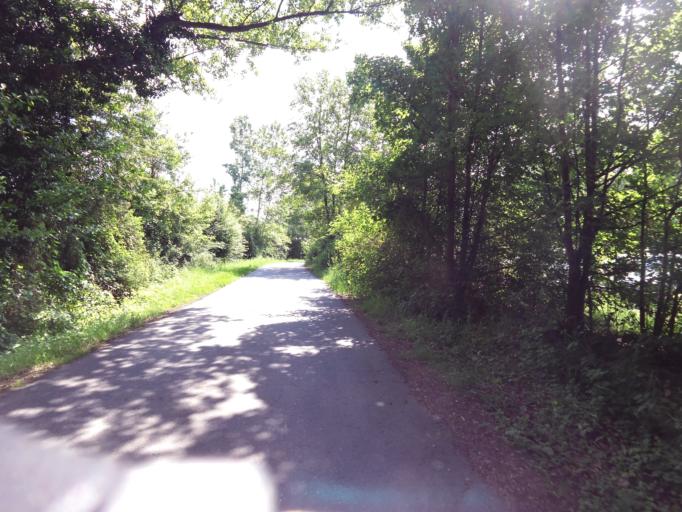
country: DE
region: Hesse
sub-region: Regierungsbezirk Darmstadt
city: Nauheim
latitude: 49.9511
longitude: 8.4715
